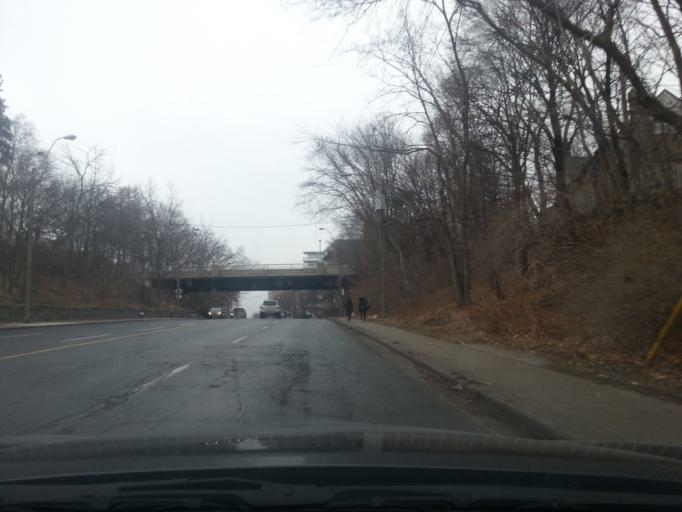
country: CA
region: Ontario
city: Toronto
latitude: 43.7017
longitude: -79.4256
